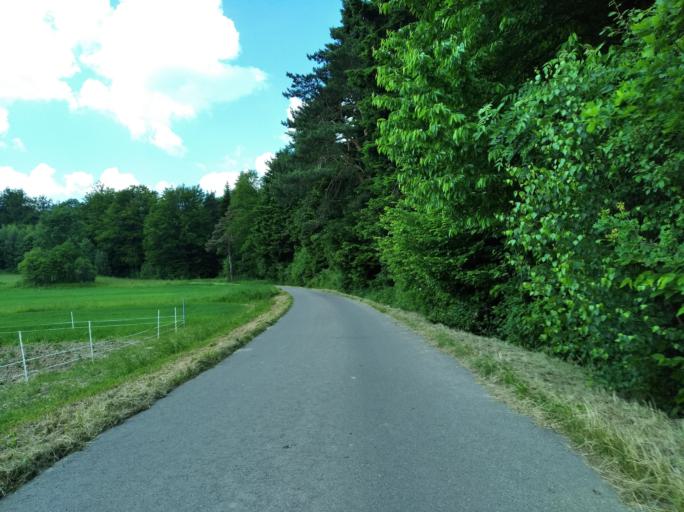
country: PL
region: Subcarpathian Voivodeship
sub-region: Powiat ropczycko-sedziszowski
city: Zagorzyce
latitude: 49.9665
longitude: 21.7121
